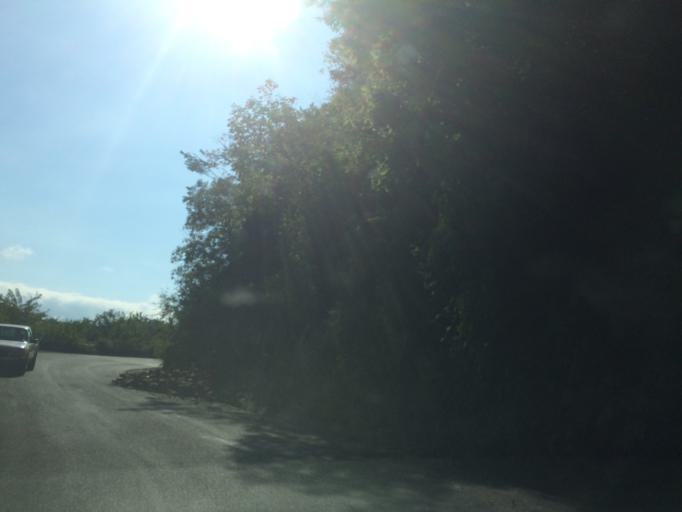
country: MX
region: Nayarit
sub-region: Ahuacatlan
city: Ahuacatlan
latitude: 21.0292
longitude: -104.4761
